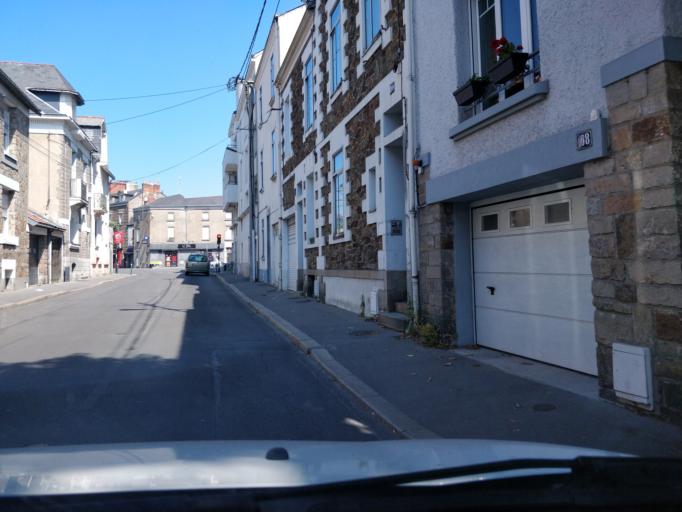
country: FR
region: Pays de la Loire
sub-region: Departement de la Loire-Atlantique
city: Nantes
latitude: 47.2267
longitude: -1.5419
